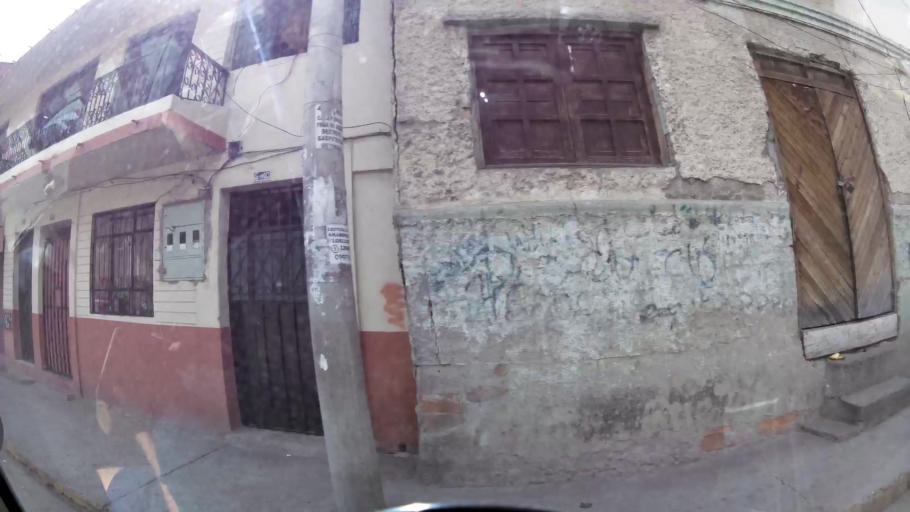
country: EC
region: Azuay
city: Cuenca
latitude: -2.8888
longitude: -78.9944
